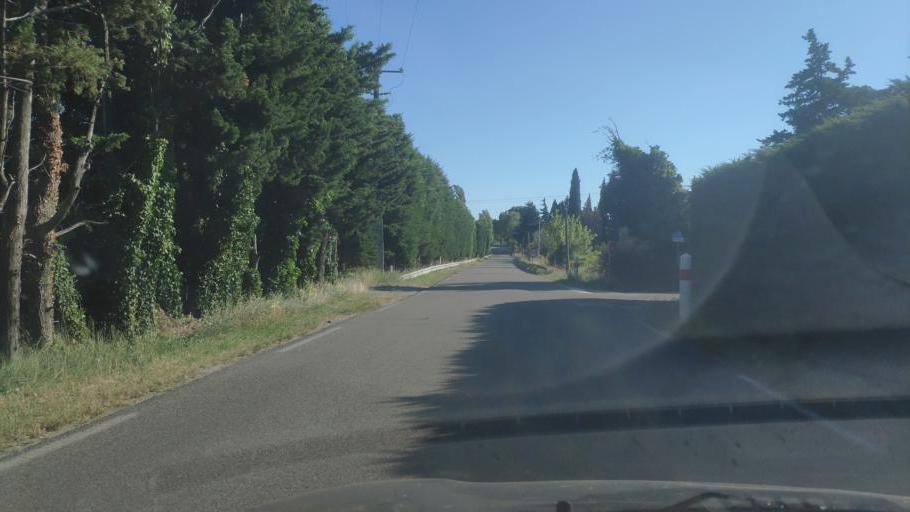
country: FR
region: Provence-Alpes-Cote d'Azur
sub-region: Departement du Vaucluse
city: Aubignan
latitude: 44.0896
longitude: 5.0226
